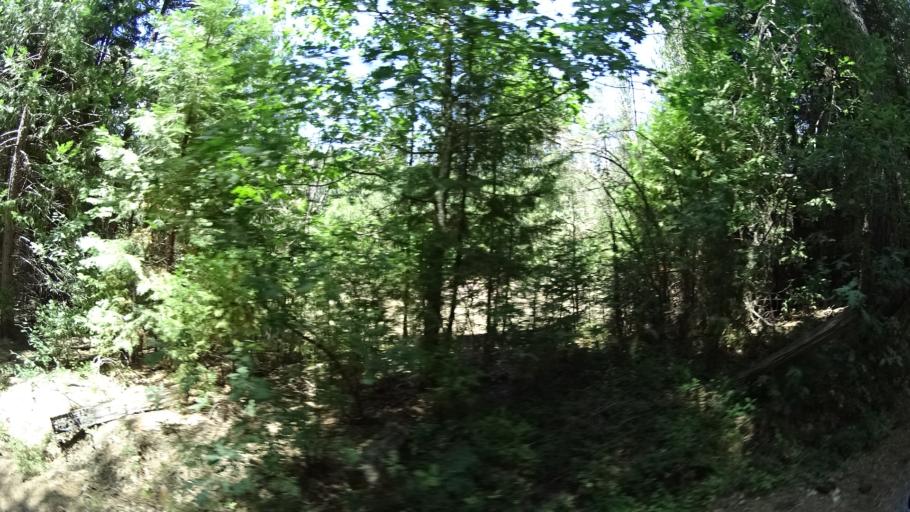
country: US
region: California
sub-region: Calaveras County
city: Arnold
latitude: 38.2592
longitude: -120.4125
